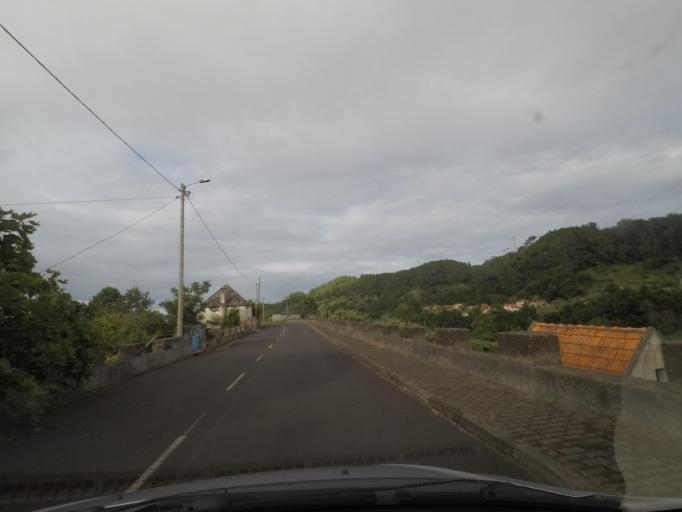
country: PT
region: Madeira
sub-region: Santana
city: Santana
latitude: 32.8007
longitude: -16.8743
